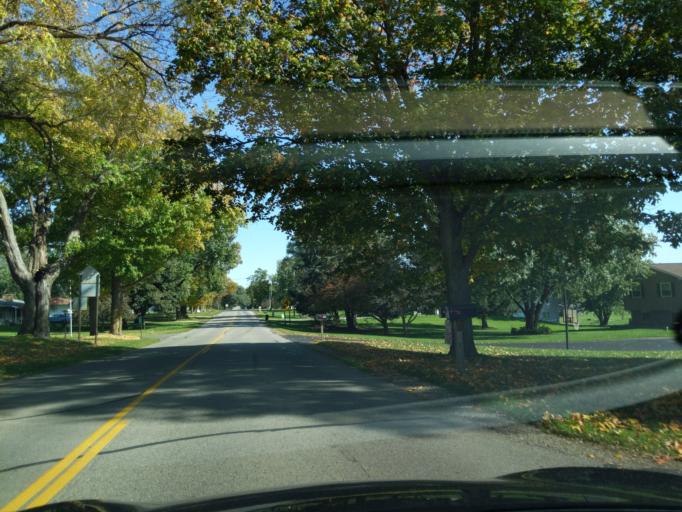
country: US
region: Michigan
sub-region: Eaton County
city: Charlotte
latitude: 42.5821
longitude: -84.8002
